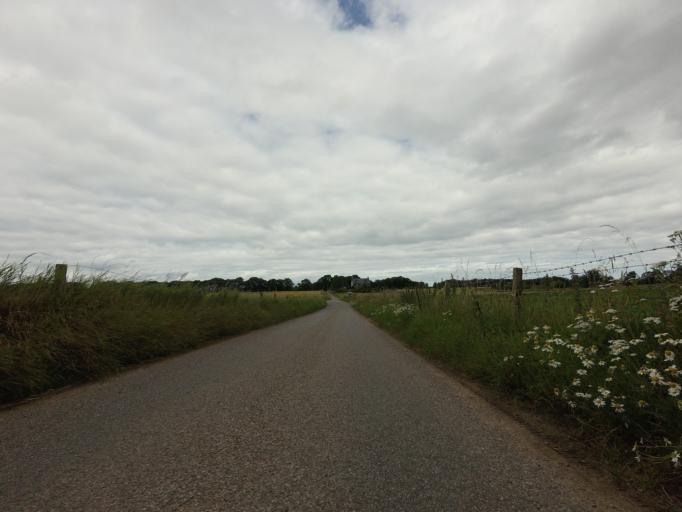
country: GB
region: Scotland
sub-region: Moray
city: Forres
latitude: 57.6253
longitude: -3.6518
